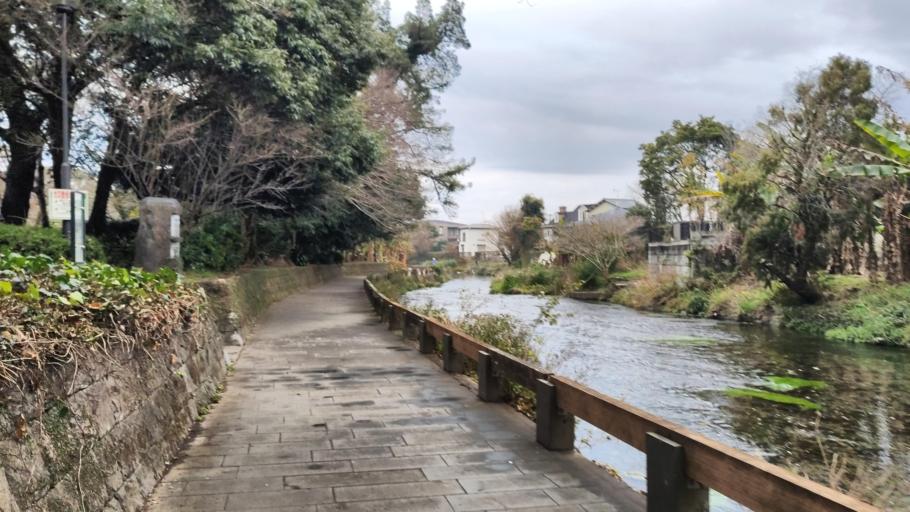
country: JP
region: Kumamoto
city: Kumamoto
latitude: 32.7861
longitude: 130.7346
